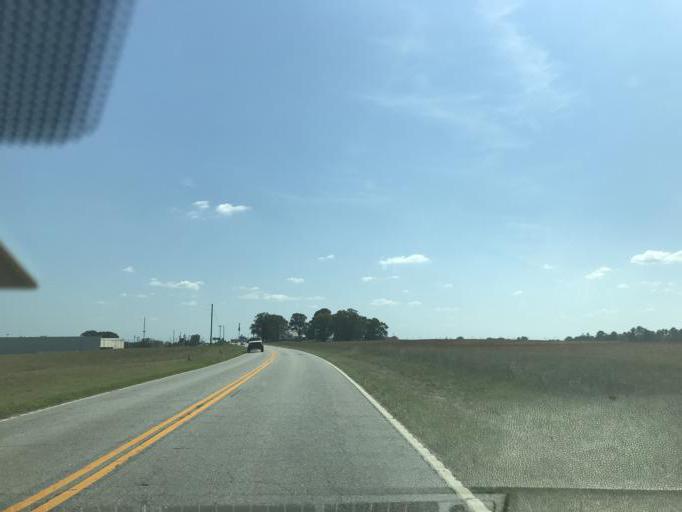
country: US
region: South Carolina
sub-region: Cherokee County
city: Gaffney
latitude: 35.0899
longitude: -81.7106
